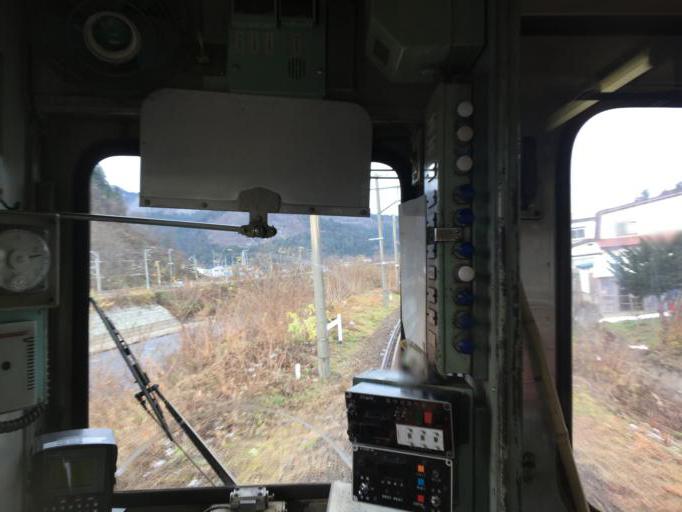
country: JP
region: Aomori
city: Hirosaki
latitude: 40.5229
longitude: 140.5602
